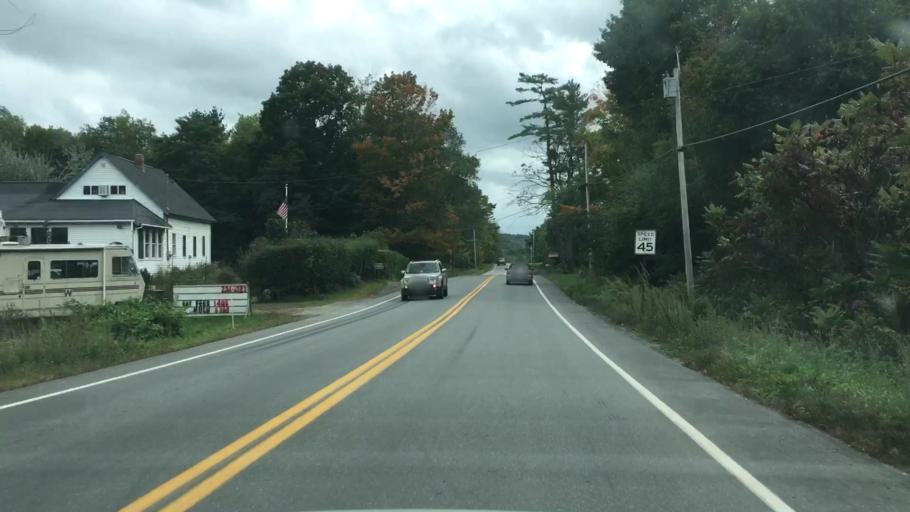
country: US
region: Maine
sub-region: Penobscot County
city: Hermon
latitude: 44.7554
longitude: -68.9729
